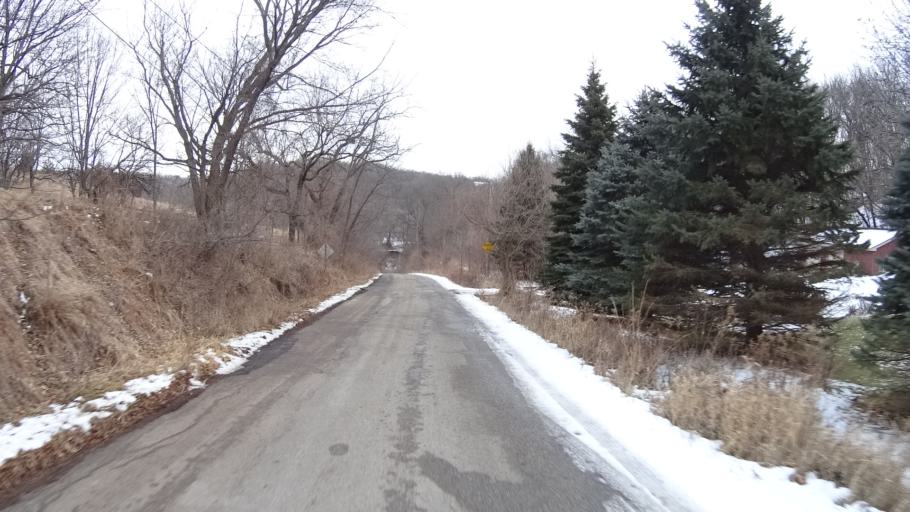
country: US
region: Nebraska
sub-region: Sarpy County
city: Bellevue
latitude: 41.1741
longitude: -95.9093
